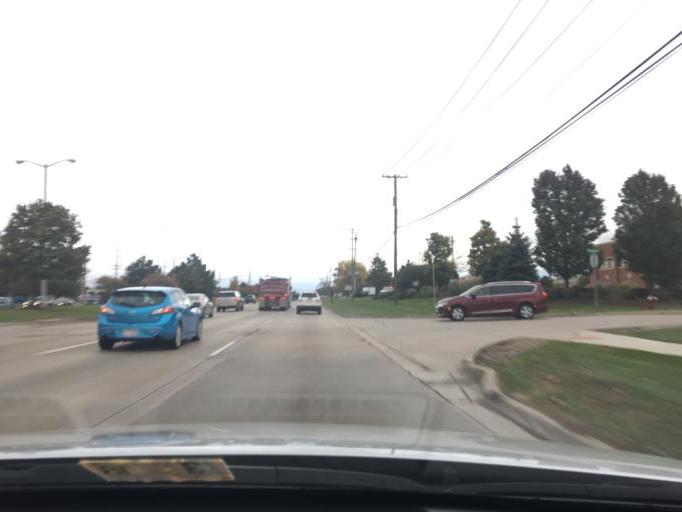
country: US
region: Michigan
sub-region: Macomb County
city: Sterling Heights
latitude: 42.5675
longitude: -83.0490
